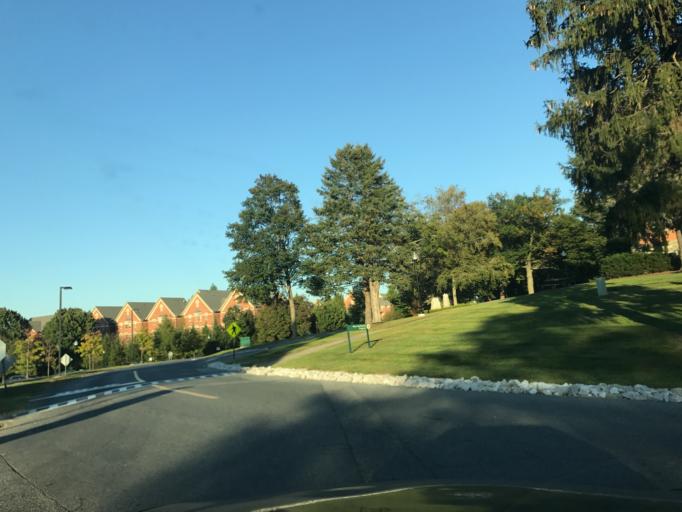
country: US
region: Maryland
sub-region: Baltimore County
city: Towson
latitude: 39.3918
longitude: -76.6218
